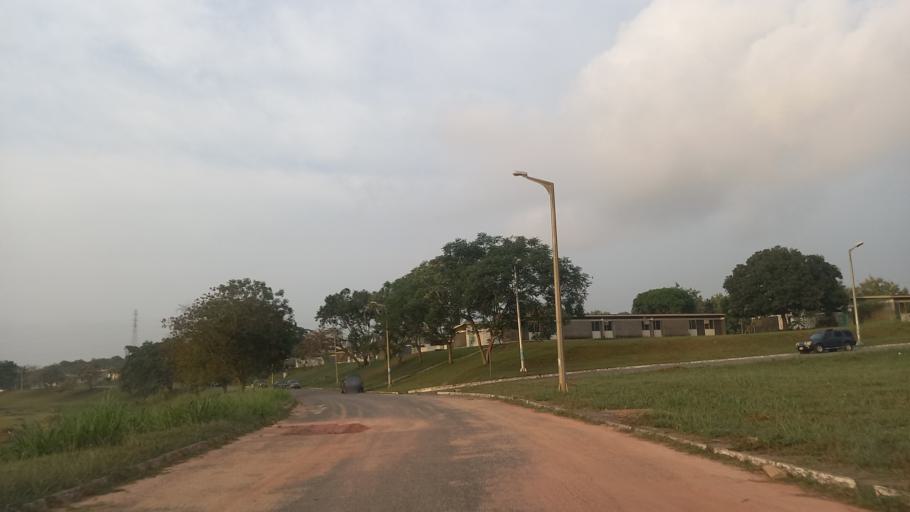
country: GH
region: Western
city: Shama Junction
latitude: 4.9840
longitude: -1.6591
